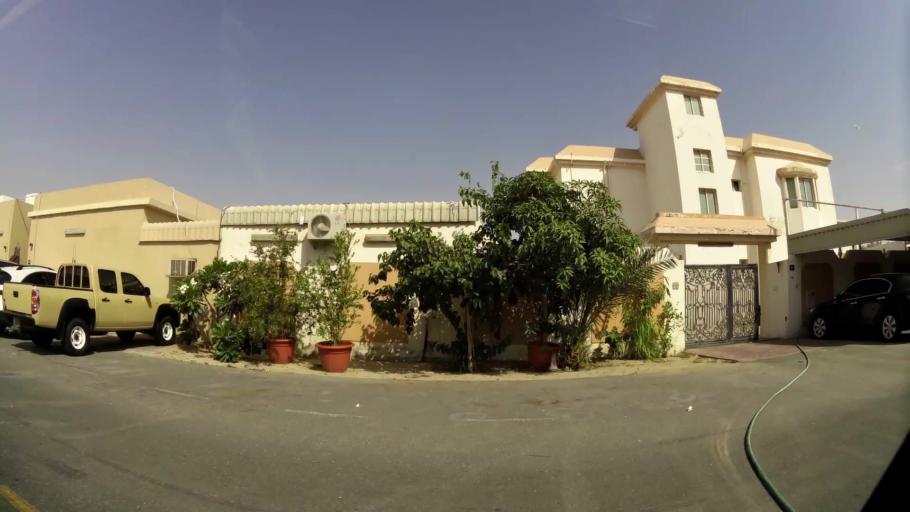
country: AE
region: Dubai
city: Dubai
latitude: 25.1667
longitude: 55.2478
